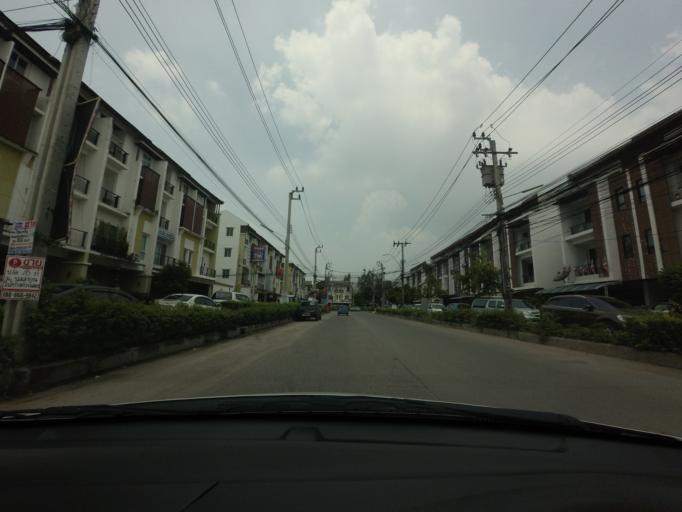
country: TH
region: Bangkok
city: Bang Na
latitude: 13.6641
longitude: 100.6909
